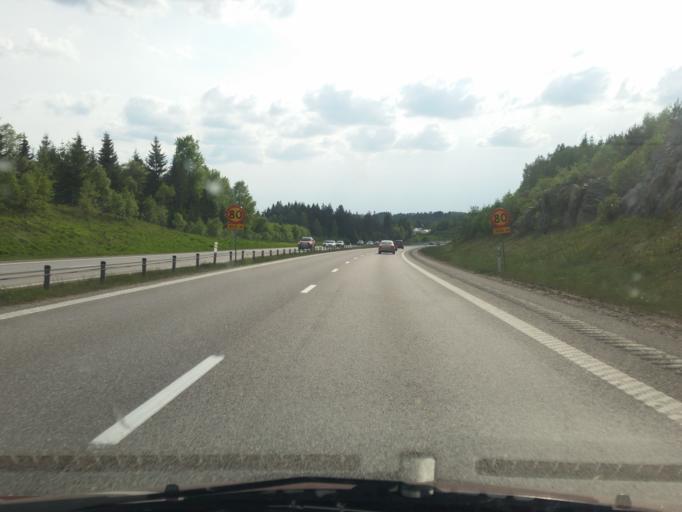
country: SE
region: Vaestra Goetaland
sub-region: Boras Kommun
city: Ganghester
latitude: 57.7303
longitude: 13.0286
